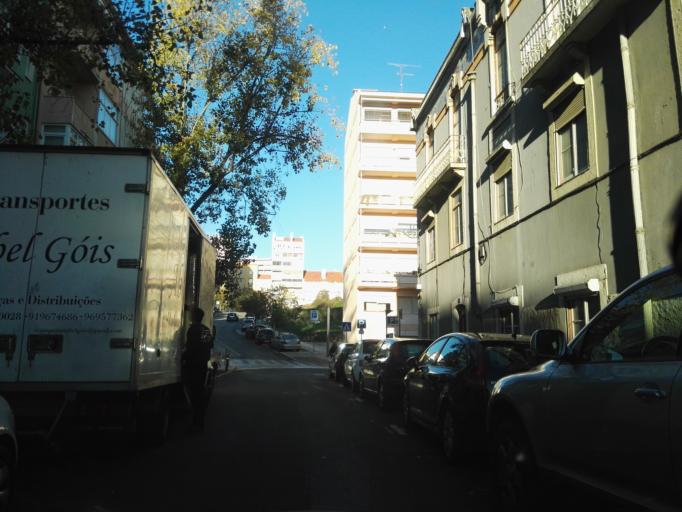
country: PT
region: Lisbon
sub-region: Lisbon
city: Lisbon
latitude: 38.7229
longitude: -9.1574
